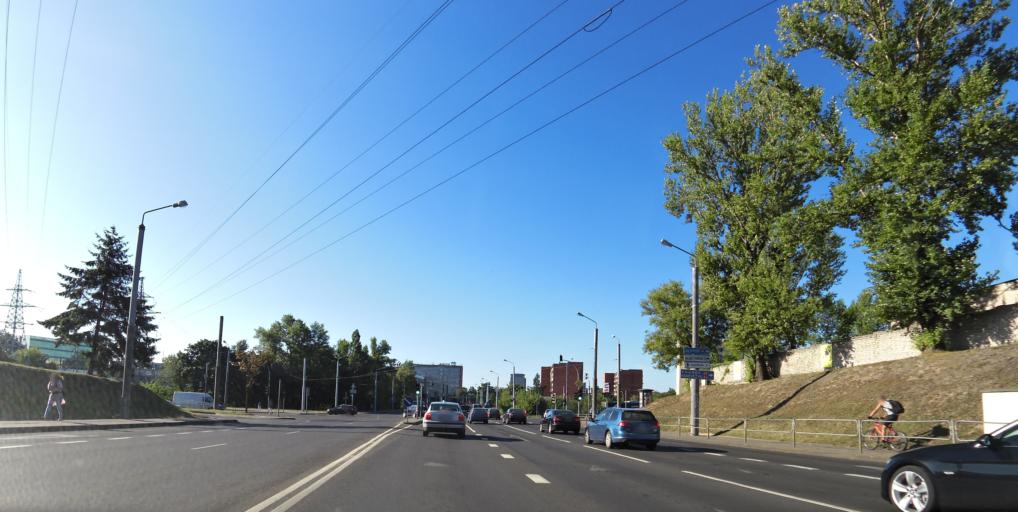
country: LT
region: Vilnius County
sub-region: Vilnius
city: Vilnius
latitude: 54.7158
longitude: 25.2868
